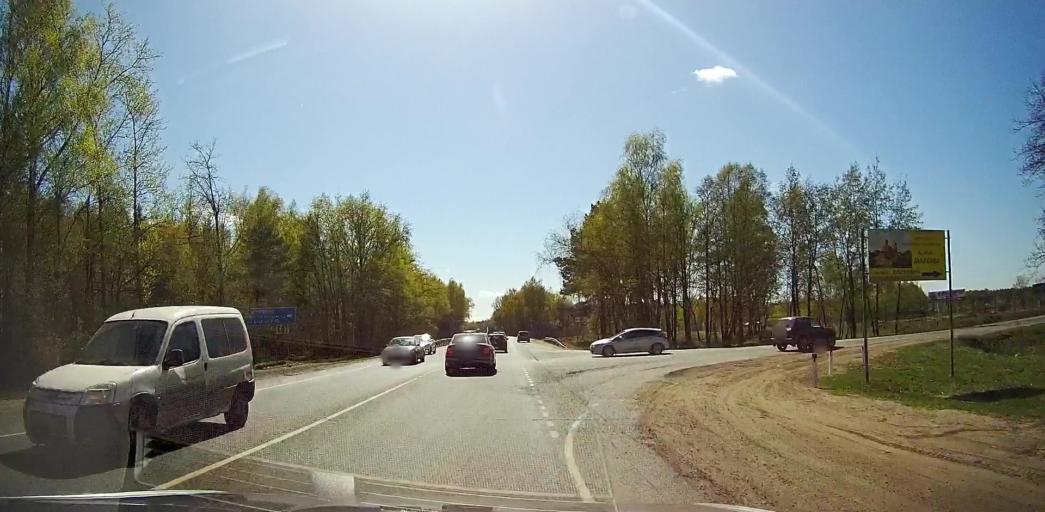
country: RU
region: Moskovskaya
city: Malyshevo
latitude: 55.4527
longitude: 38.3259
